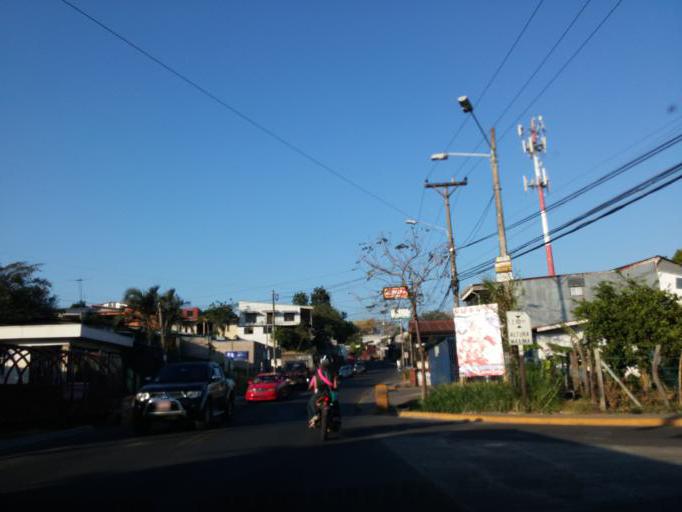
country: CR
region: Alajuela
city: Alajuela
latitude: 10.0032
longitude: -84.2190
